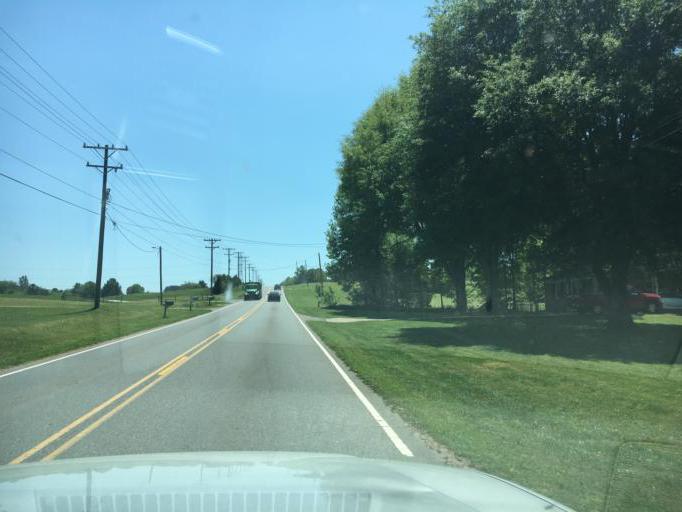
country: US
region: North Carolina
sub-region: Cleveland County
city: Shelby
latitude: 35.2373
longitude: -81.5663
